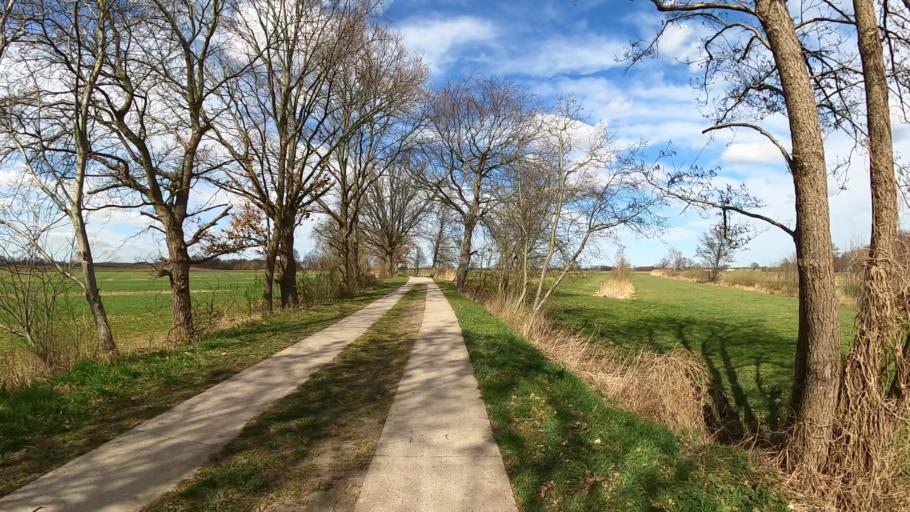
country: DE
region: Lower Saxony
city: Winsen
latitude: 53.4137
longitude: 10.1824
